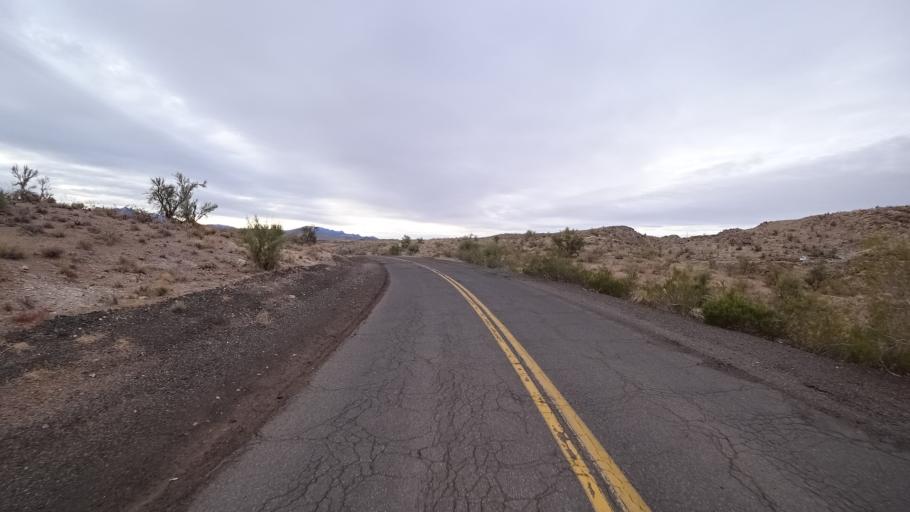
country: US
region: Arizona
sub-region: Mohave County
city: Kingman
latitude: 35.2037
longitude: -114.0827
